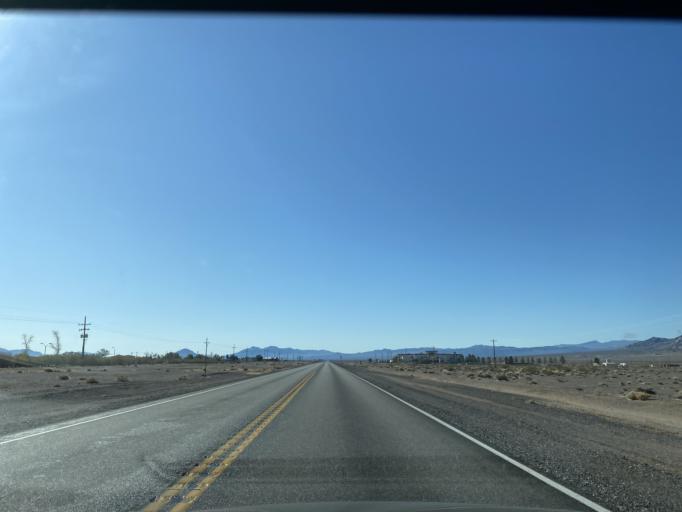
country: US
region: Nevada
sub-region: Nye County
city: Pahrump
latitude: 36.4188
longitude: -116.4222
